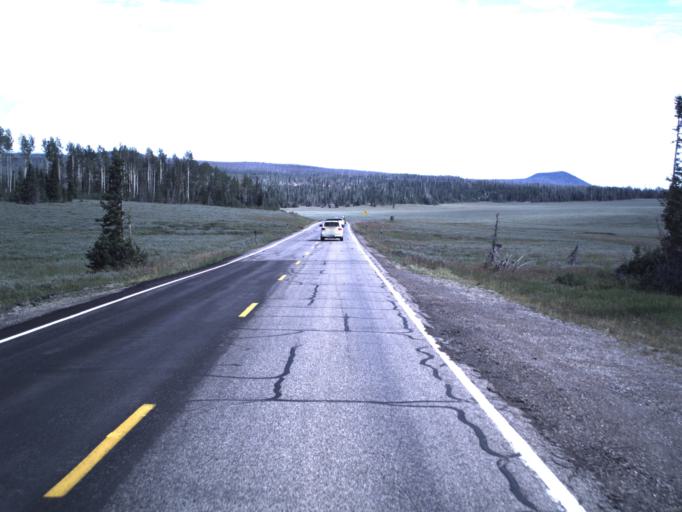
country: US
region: Utah
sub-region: Iron County
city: Parowan
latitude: 37.5609
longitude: -112.7895
